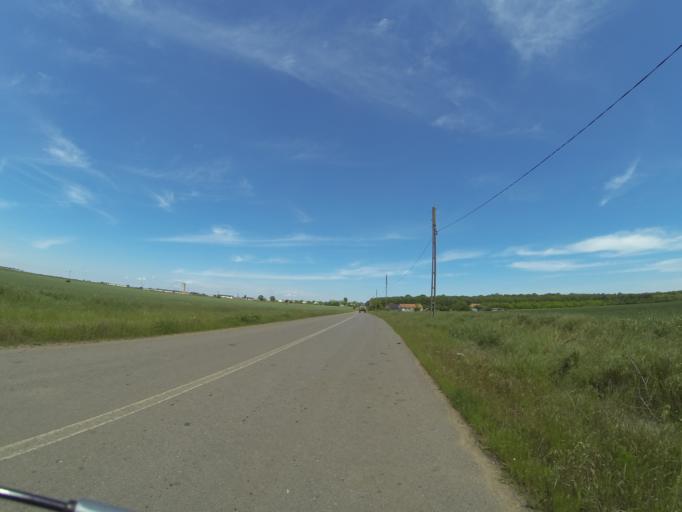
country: RO
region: Dolj
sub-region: Comuna Teslui
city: Teslui
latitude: 44.1654
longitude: 24.1600
